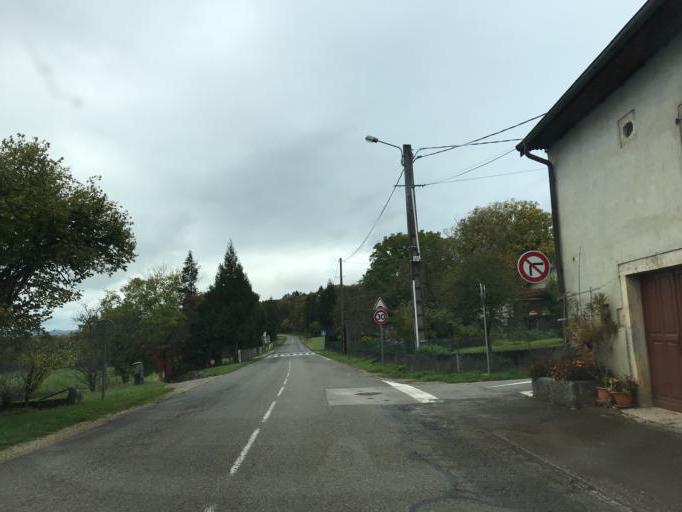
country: FR
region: Franche-Comte
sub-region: Departement du Jura
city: Arinthod
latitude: 46.4632
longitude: 5.5597
